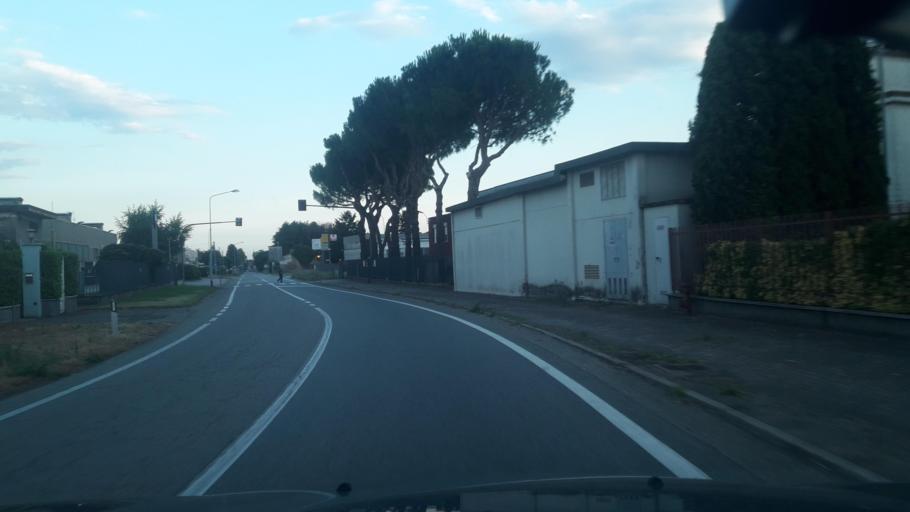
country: IT
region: Lombardy
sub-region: Citta metropolitana di Milano
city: Cuggiono
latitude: 45.5188
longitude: 8.8086
